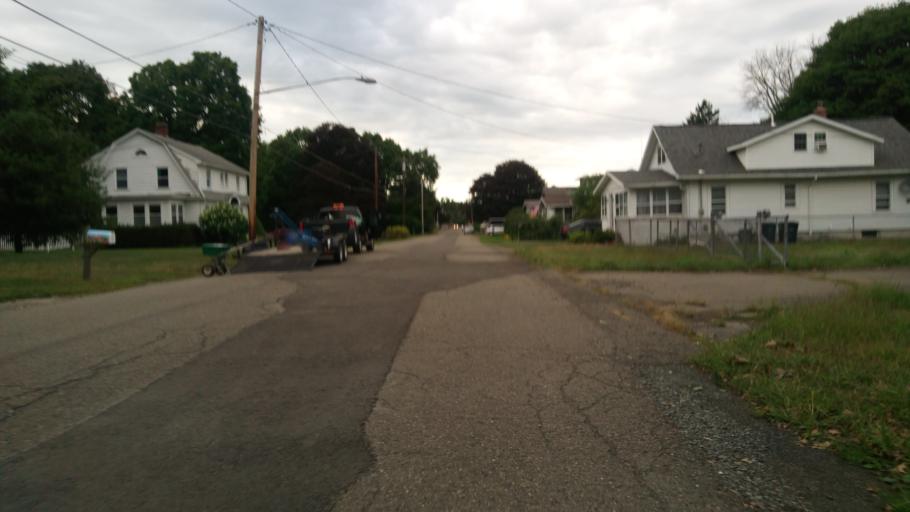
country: US
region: New York
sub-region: Chemung County
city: Southport
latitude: 42.0607
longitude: -76.8134
